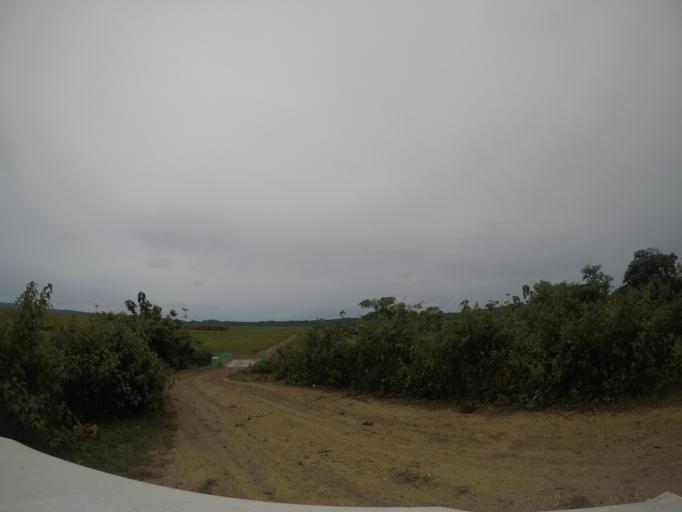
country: TL
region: Lautem
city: Lospalos
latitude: -8.5288
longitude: 127.0147
